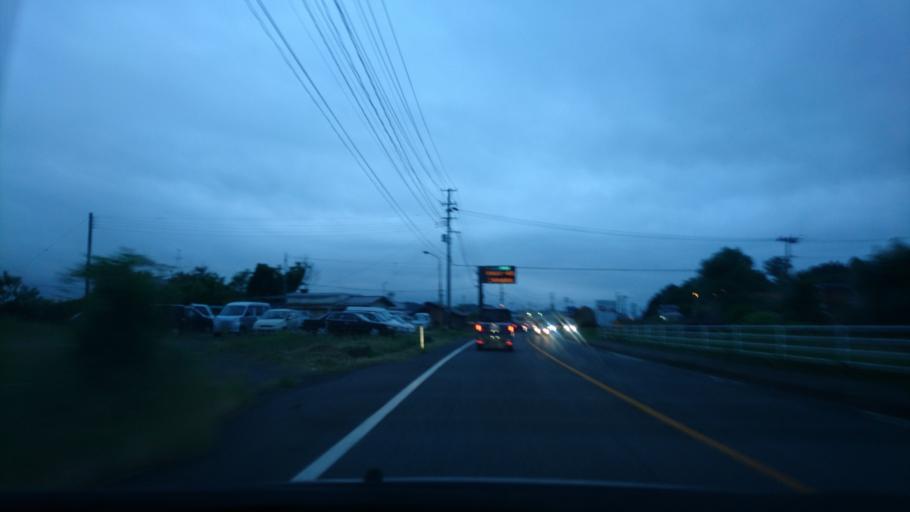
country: JP
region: Iwate
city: Ichinoseki
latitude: 38.8070
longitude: 141.0742
